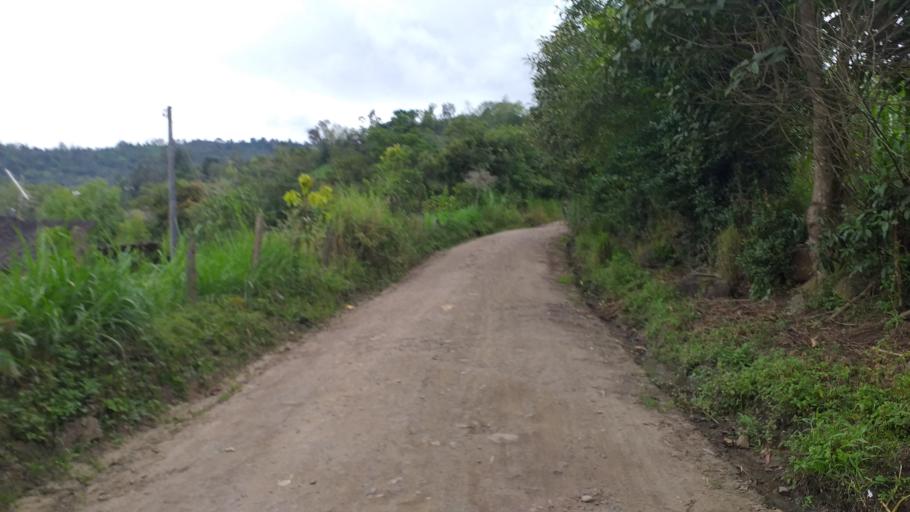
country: CO
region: Cundinamarca
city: Tenza
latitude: 5.1001
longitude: -73.4482
